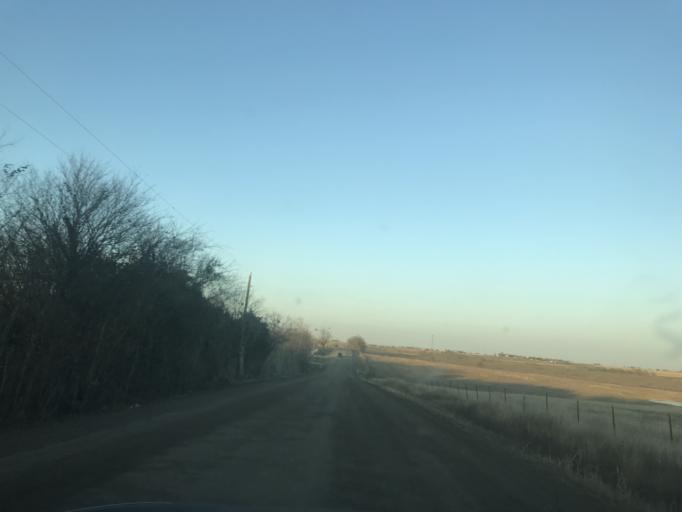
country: US
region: Texas
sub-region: Travis County
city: Pflugerville
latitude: 30.4321
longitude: -97.5286
